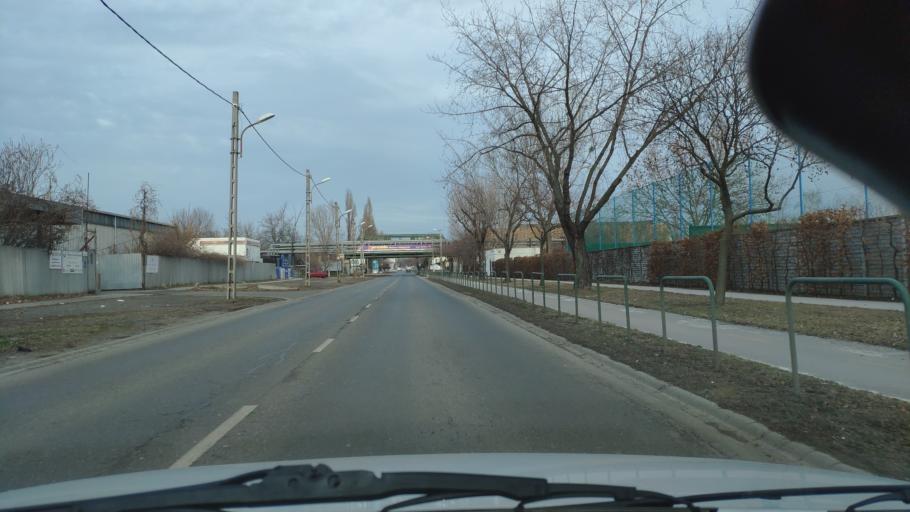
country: HU
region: Budapest
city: Budapest XIX. keruelet
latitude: 47.4702
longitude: 19.1295
